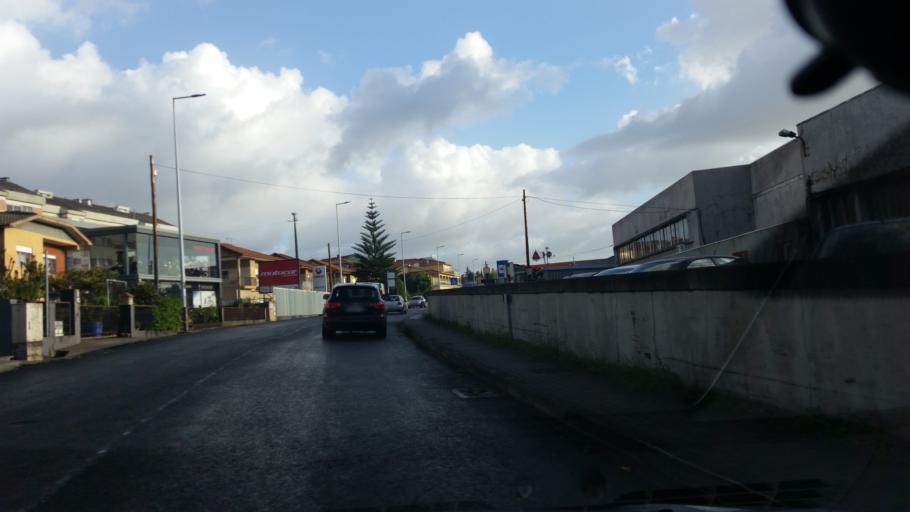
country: PT
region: Porto
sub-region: Santo Tirso
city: Negrelos
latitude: 41.3623
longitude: -8.3995
